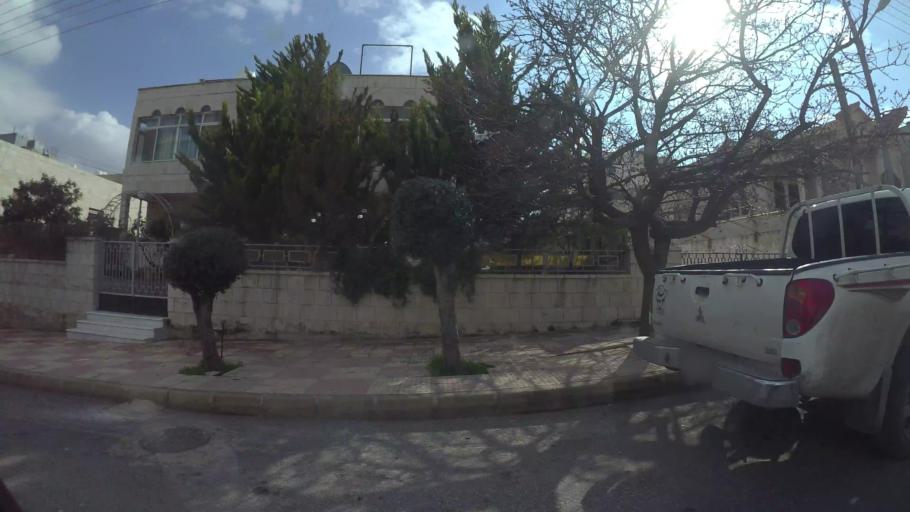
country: JO
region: Amman
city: Al Jubayhah
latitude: 32.0175
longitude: 35.8637
